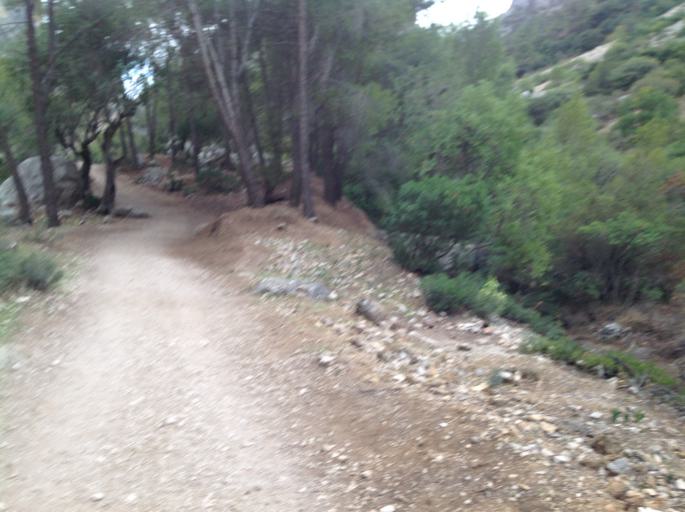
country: ES
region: Andalusia
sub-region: Provincia de Malaga
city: Ardales
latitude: 36.9225
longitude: -4.7811
